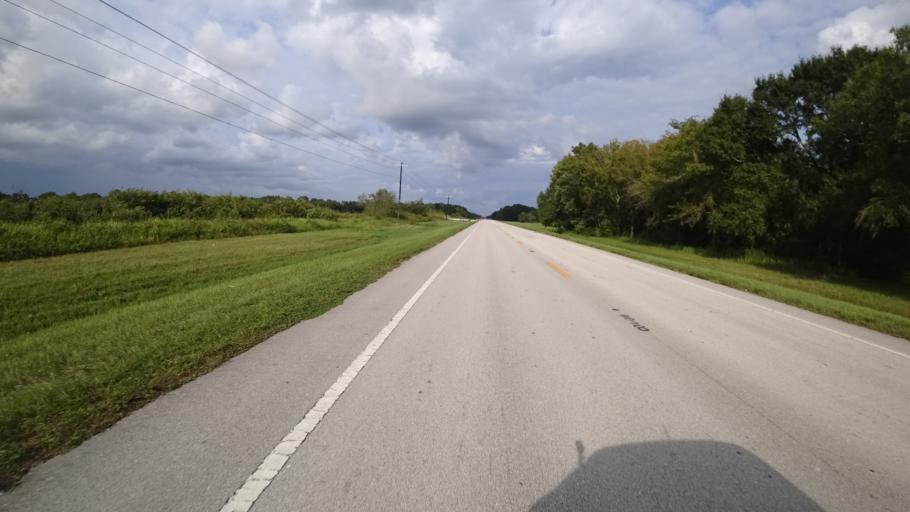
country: US
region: Florida
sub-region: Hillsborough County
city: Ruskin
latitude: 27.6110
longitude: -82.4154
